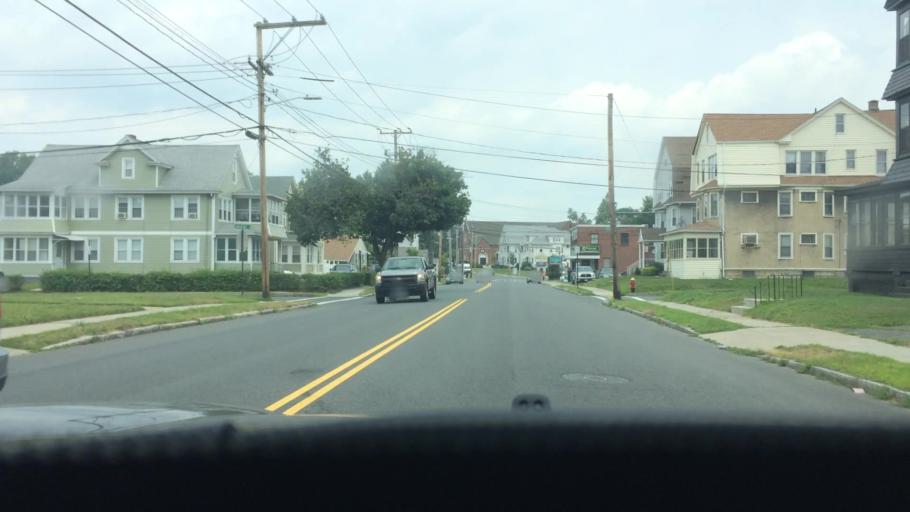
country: US
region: Massachusetts
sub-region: Hampden County
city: Chicopee
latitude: 42.1459
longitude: -72.5799
